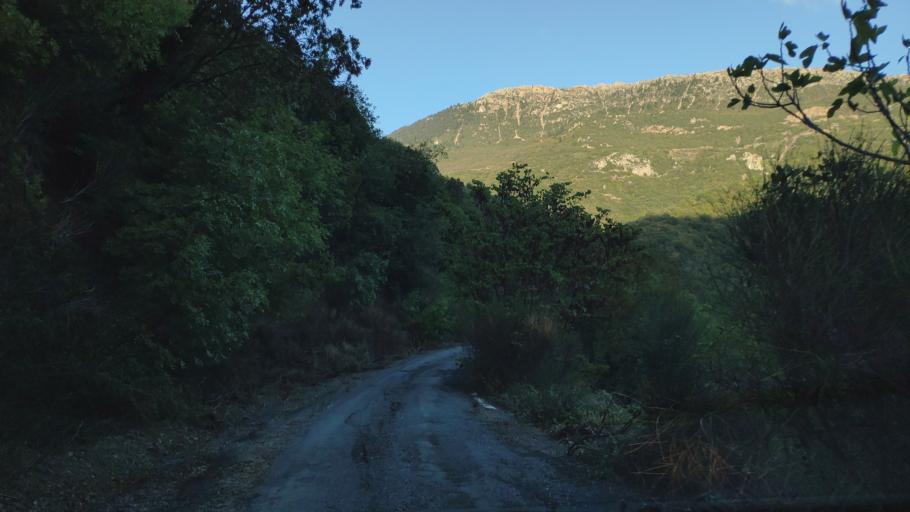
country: GR
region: Peloponnese
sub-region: Nomos Arkadias
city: Dimitsana
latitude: 37.5619
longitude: 22.0418
